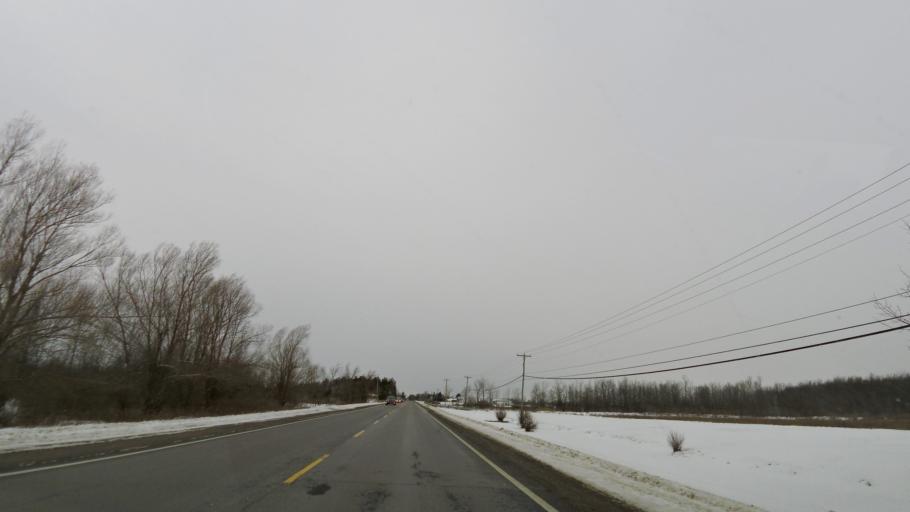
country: CA
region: Ontario
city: Cambridge
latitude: 43.3195
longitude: -80.1858
